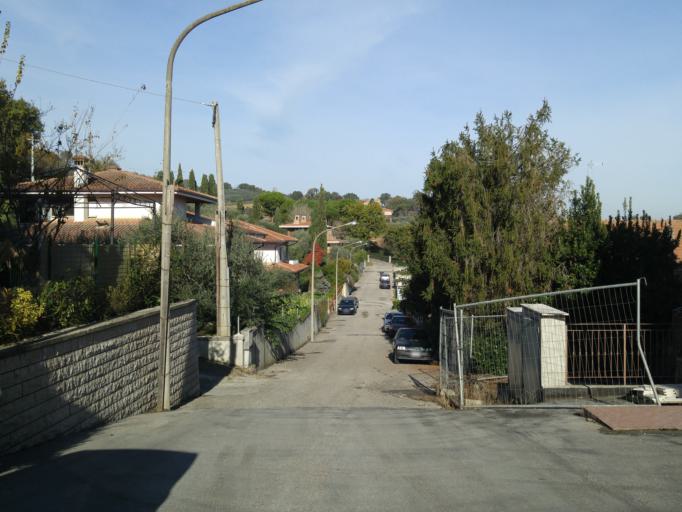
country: IT
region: The Marches
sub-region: Provincia di Pesaro e Urbino
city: Saltara
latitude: 43.7516
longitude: 12.8954
